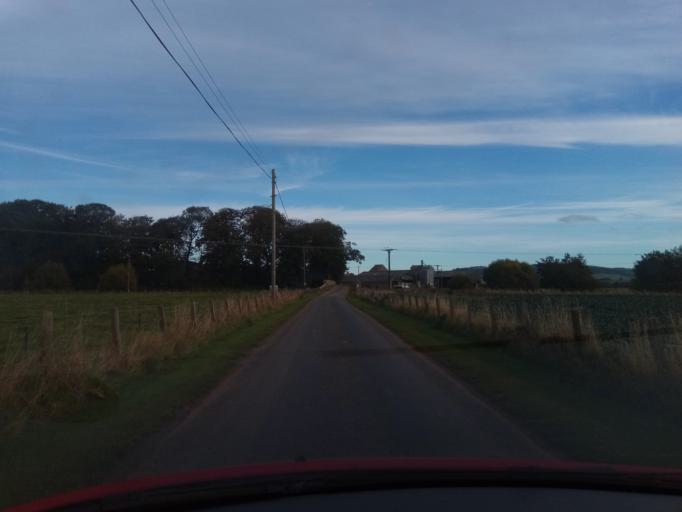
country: GB
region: Scotland
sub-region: The Scottish Borders
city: Kelso
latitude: 55.5233
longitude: -2.3999
